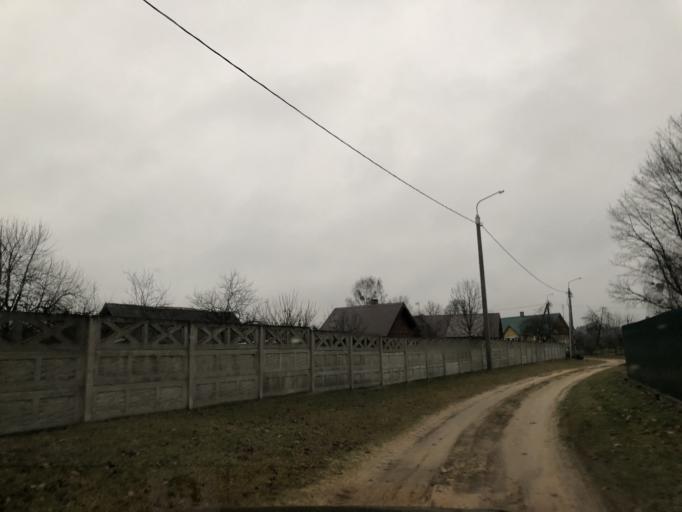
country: LT
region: Alytaus apskritis
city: Druskininkai
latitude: 53.9109
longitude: 24.1774
